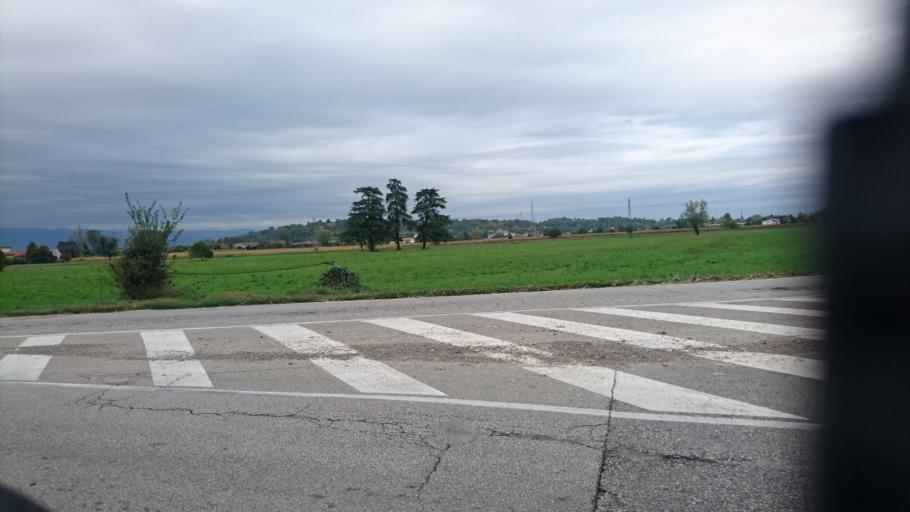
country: IT
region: Veneto
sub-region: Provincia di Vicenza
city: Creazzo
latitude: 45.5480
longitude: 11.4922
